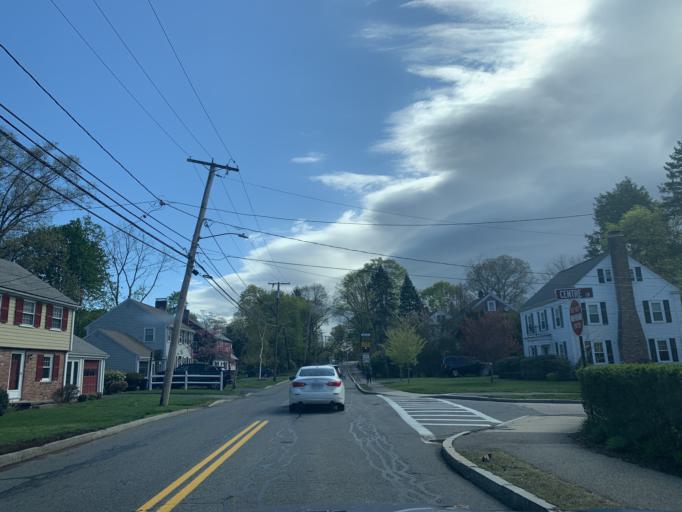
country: US
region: Massachusetts
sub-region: Norfolk County
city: Milton
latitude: 42.2551
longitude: -71.0764
